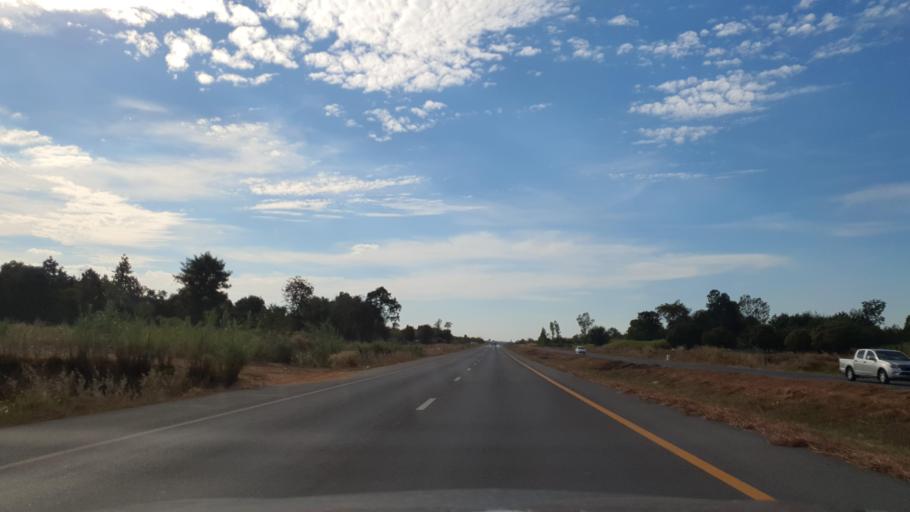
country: TH
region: Roi Et
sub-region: Amphoe Pho Chai
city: Pho Chai
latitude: 16.4130
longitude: 103.7764
